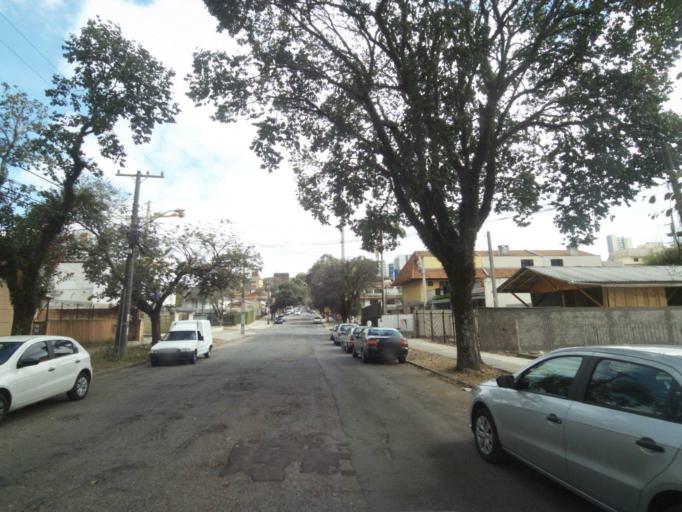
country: BR
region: Parana
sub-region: Curitiba
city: Curitiba
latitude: -25.4659
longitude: -49.2869
